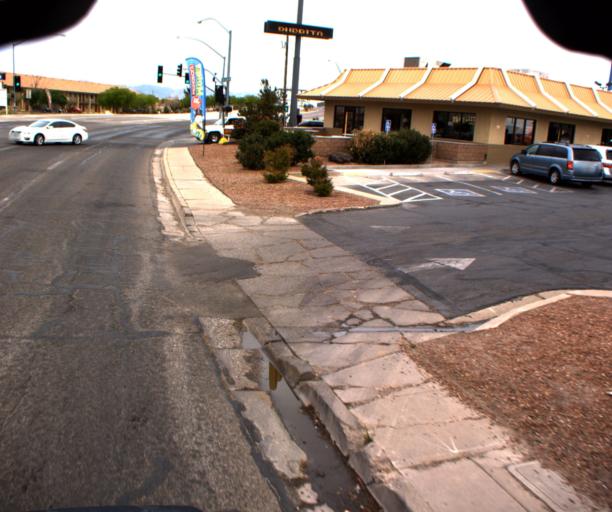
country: US
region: Arizona
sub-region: Cochise County
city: Willcox
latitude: 32.2644
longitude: -109.8408
